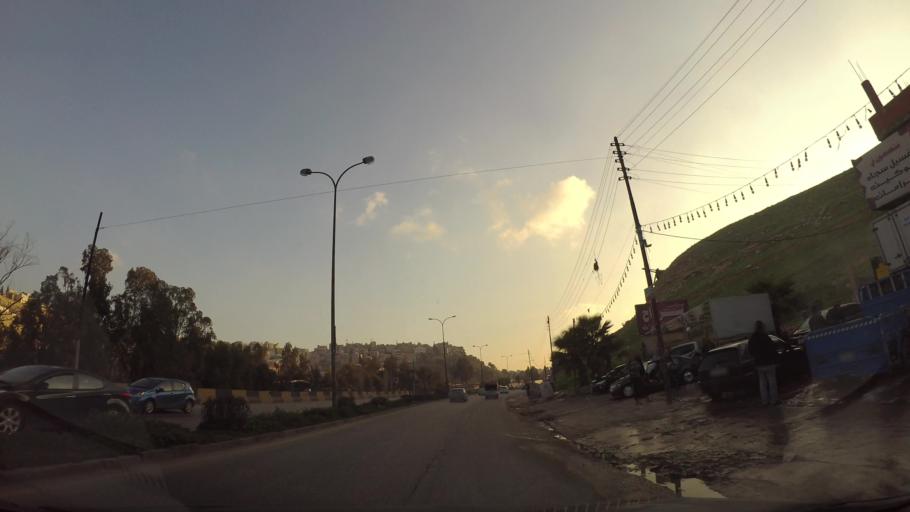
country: JO
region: Amman
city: Amman
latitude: 31.9838
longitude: 35.9760
